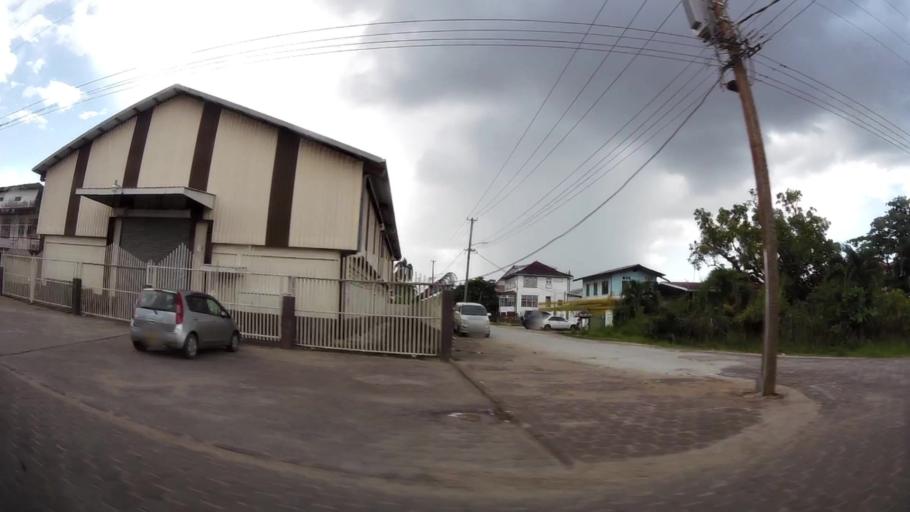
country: SR
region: Paramaribo
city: Paramaribo
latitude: 5.8306
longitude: -55.1471
